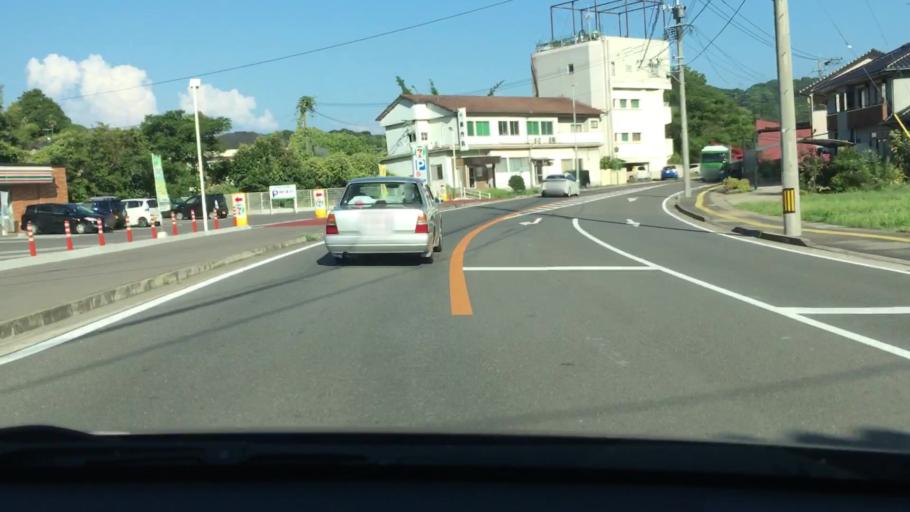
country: JP
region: Nagasaki
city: Togitsu
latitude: 32.9872
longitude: 129.7743
